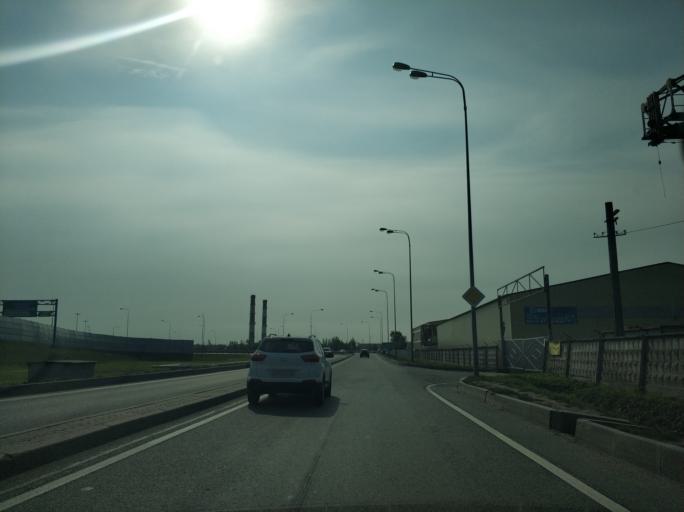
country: RU
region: Leningrad
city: Murino
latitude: 60.0363
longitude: 30.4391
